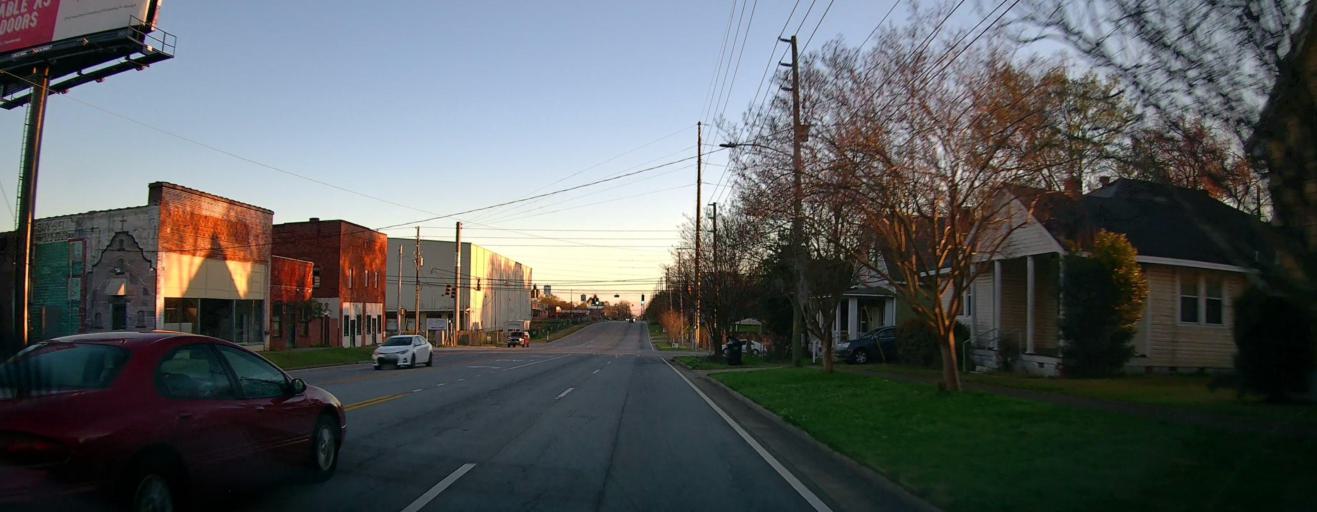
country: US
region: Alabama
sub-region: Russell County
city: Phenix City
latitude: 32.4971
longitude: -84.9902
